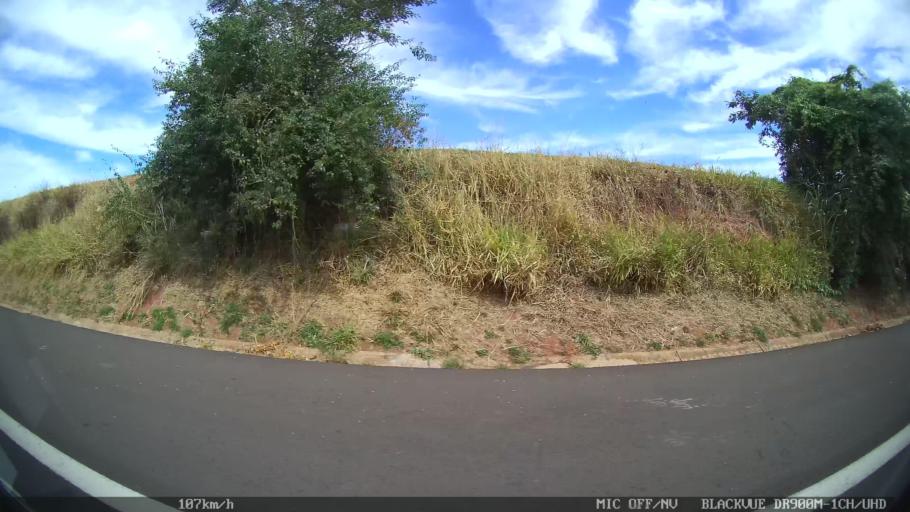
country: BR
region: Sao Paulo
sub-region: Taquaritinga
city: Taquaritinga
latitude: -21.4544
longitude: -48.6295
